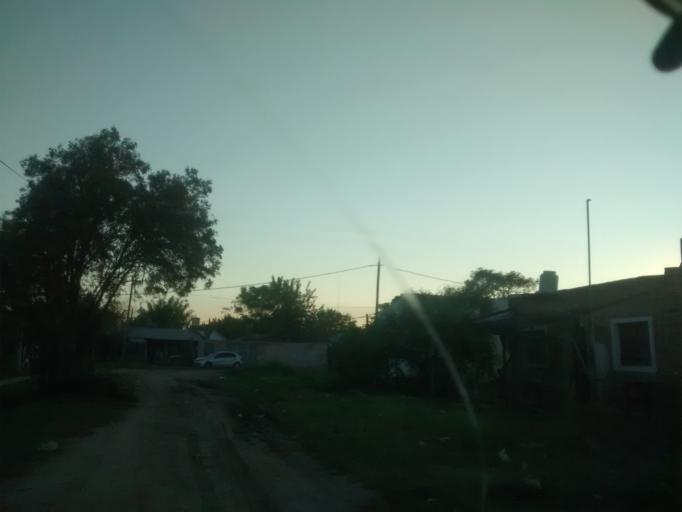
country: AR
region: Chaco
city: Fontana
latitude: -27.3967
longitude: -58.9917
